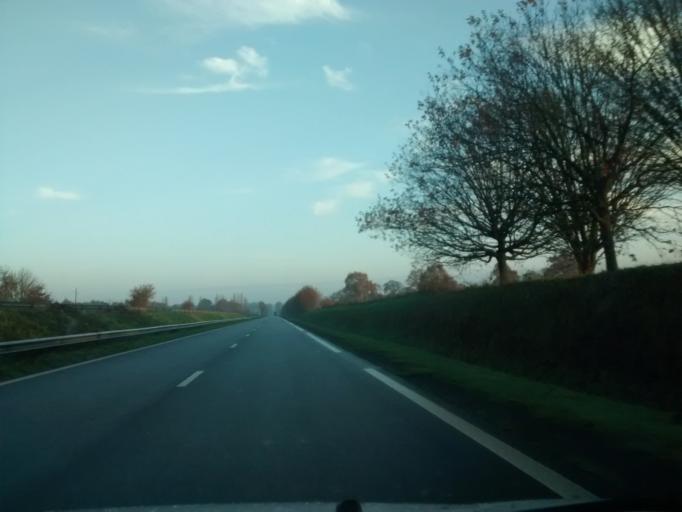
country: FR
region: Brittany
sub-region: Departement d'Ille-et-Vilaine
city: Chevaigne
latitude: 48.2185
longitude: -1.6233
